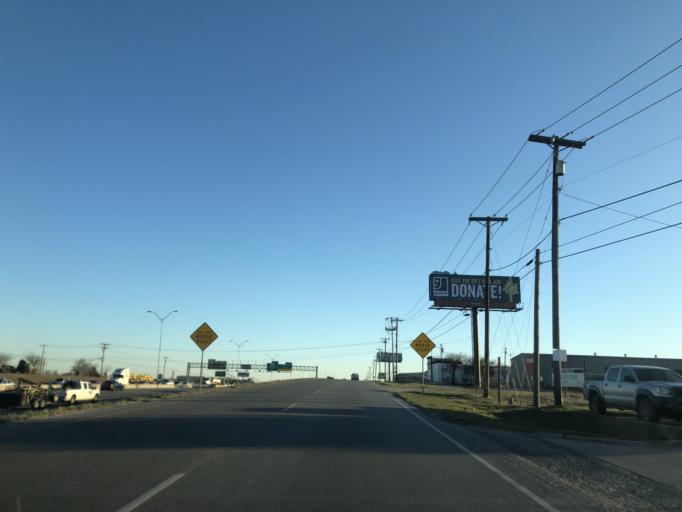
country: US
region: Texas
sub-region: Travis County
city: Windemere
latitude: 30.4667
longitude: -97.6701
